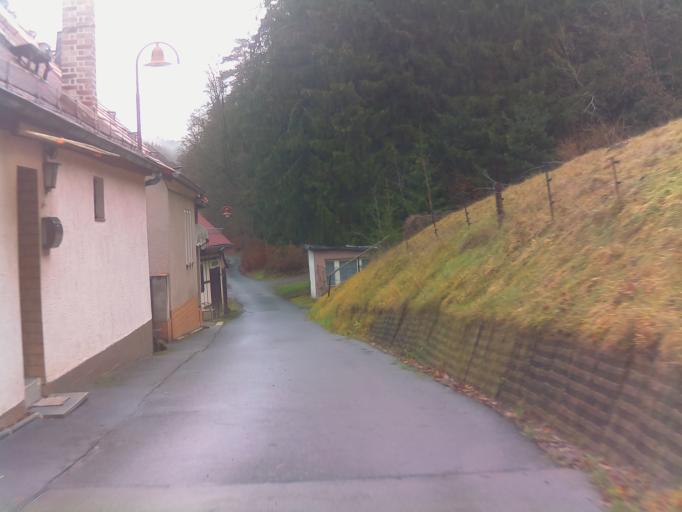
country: DE
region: Thuringia
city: Hummelshain
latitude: 50.7475
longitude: 11.6414
